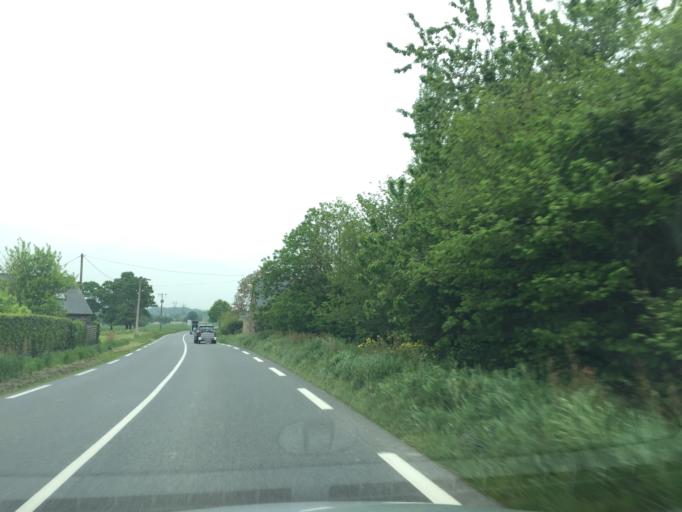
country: FR
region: Brittany
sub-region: Departement des Cotes-d'Armor
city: Henanbihen
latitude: 48.5169
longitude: -2.4460
